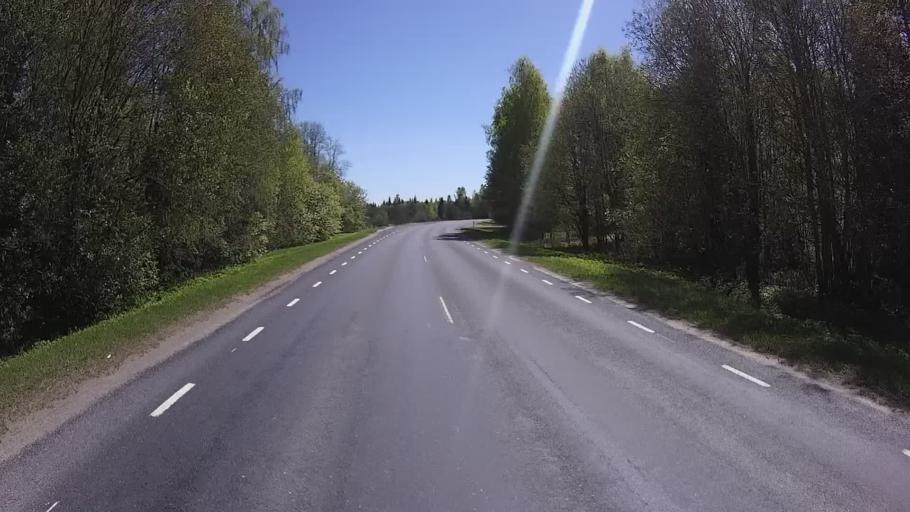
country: EE
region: Harju
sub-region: Raasiku vald
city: Raasiku
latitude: 59.1461
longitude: 25.2010
